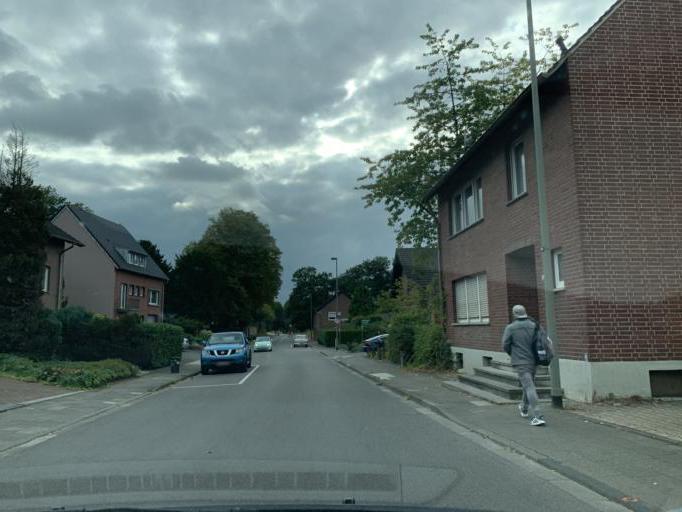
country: DE
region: North Rhine-Westphalia
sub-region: Regierungsbezirk Koln
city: Wassenberg
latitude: 51.0951
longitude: 6.1862
